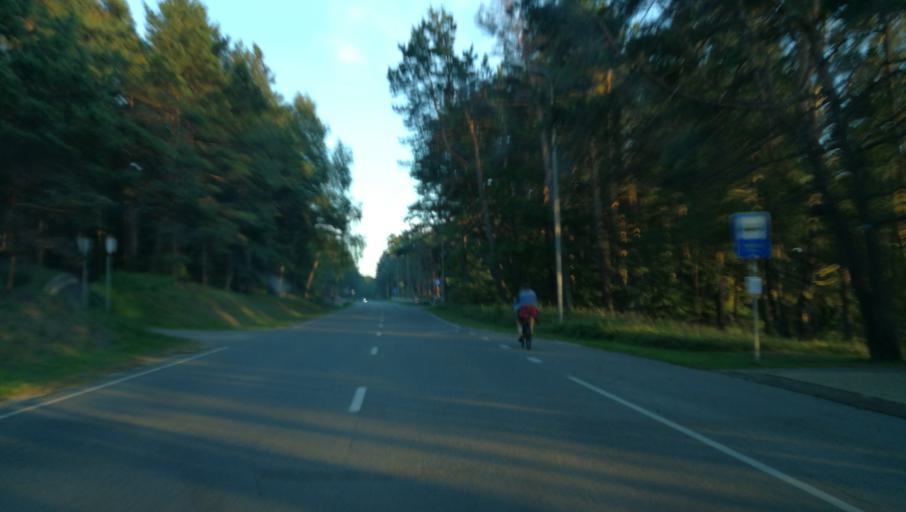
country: LV
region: Saulkrastu
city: Saulkrasti
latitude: 57.2854
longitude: 24.4138
